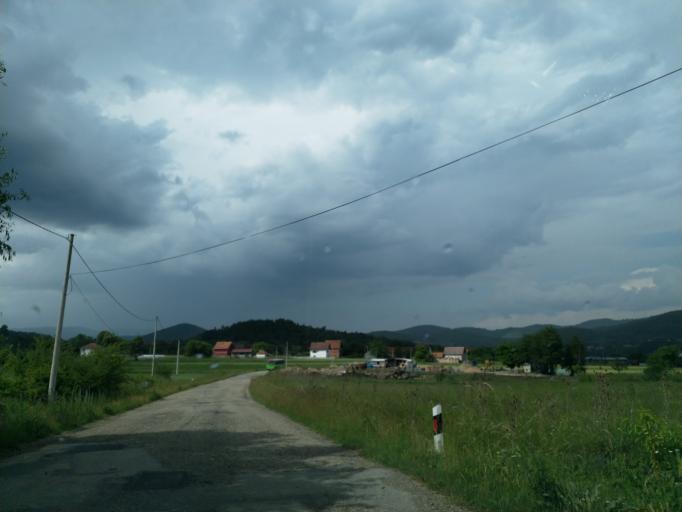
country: RS
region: Central Serbia
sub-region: Borski Okrug
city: Bor
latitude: 44.0006
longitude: 21.9792
